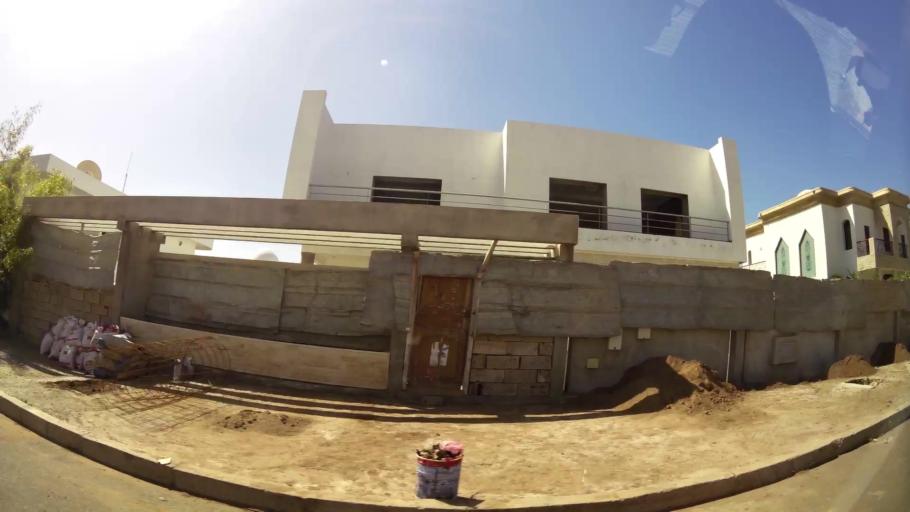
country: MA
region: Souss-Massa-Draa
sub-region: Agadir-Ida-ou-Tnan
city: Agadir
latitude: 30.4420
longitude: -9.5873
